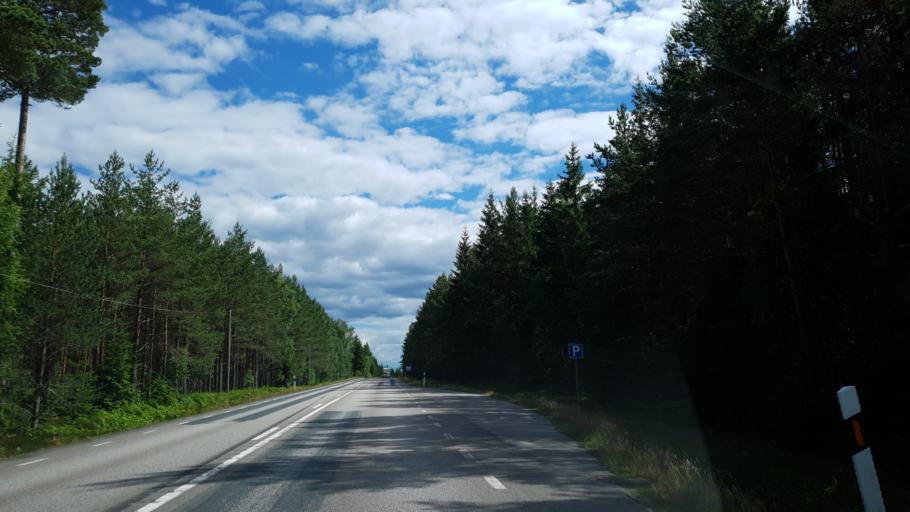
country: SE
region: Kronoberg
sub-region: Uppvidinge Kommun
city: Lenhovda
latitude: 56.8777
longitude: 15.3811
